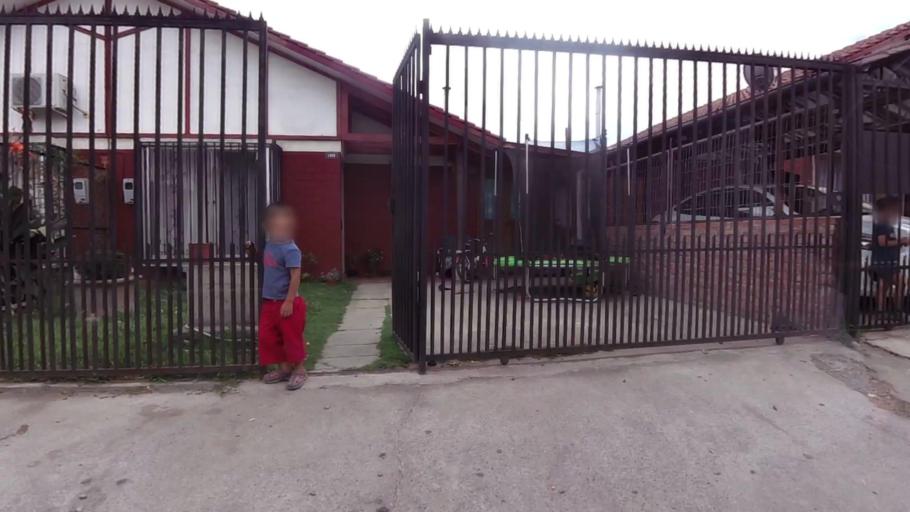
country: CL
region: O'Higgins
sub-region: Provincia de Cachapoal
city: Graneros
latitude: -34.0653
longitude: -70.7237
